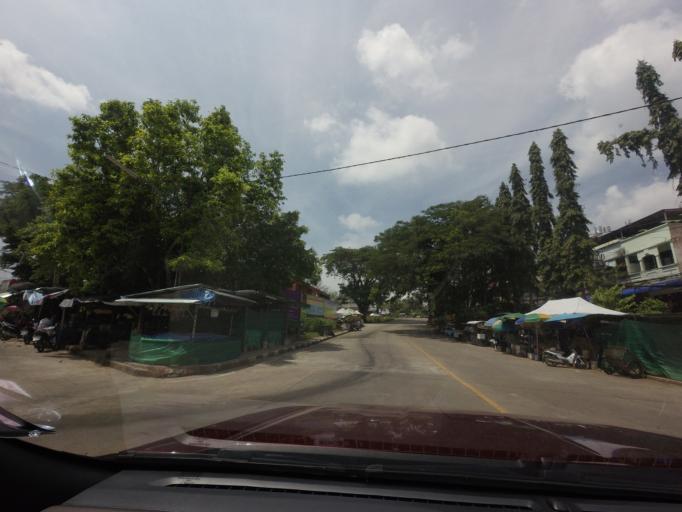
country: TH
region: Yala
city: Betong
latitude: 5.7690
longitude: 101.0748
